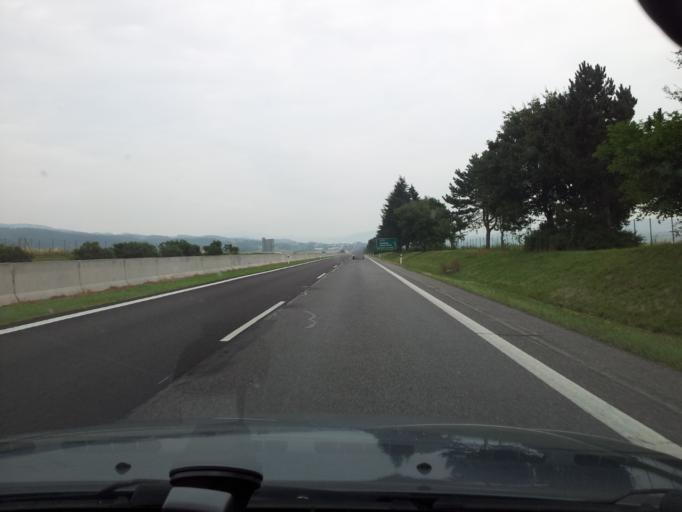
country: SK
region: Banskobystricky
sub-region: Okres Banska Bystrica
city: Zvolen
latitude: 48.6330
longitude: 19.1196
